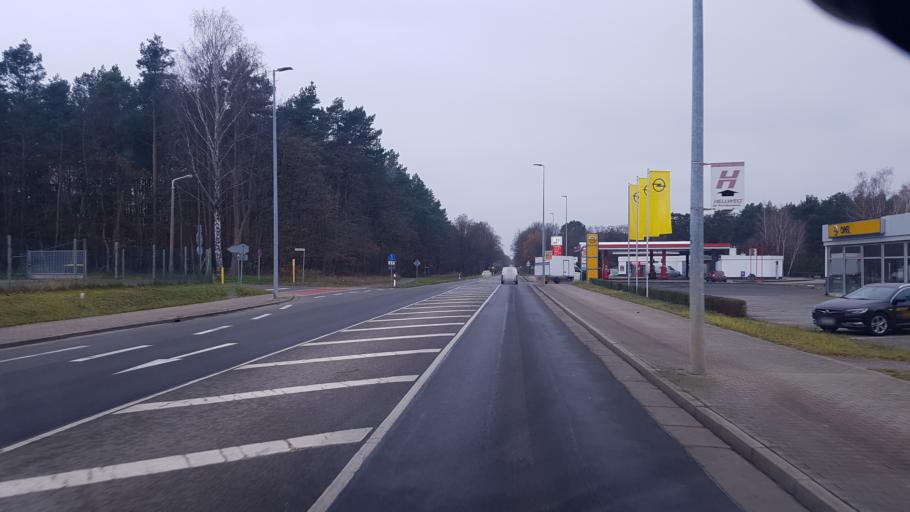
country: DE
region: Brandenburg
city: Guben
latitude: 51.9567
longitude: 14.6764
